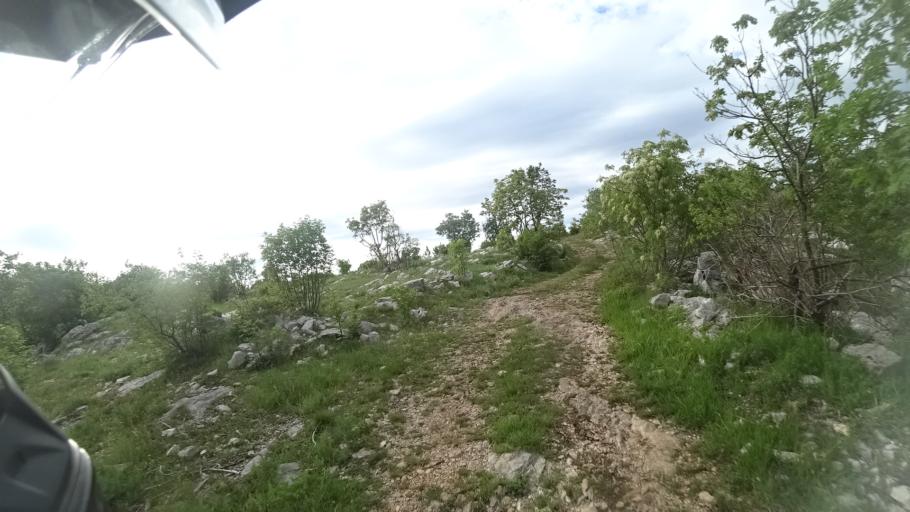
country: HR
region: Sibensko-Kniniska
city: Drnis
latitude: 43.8630
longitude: 16.3930
